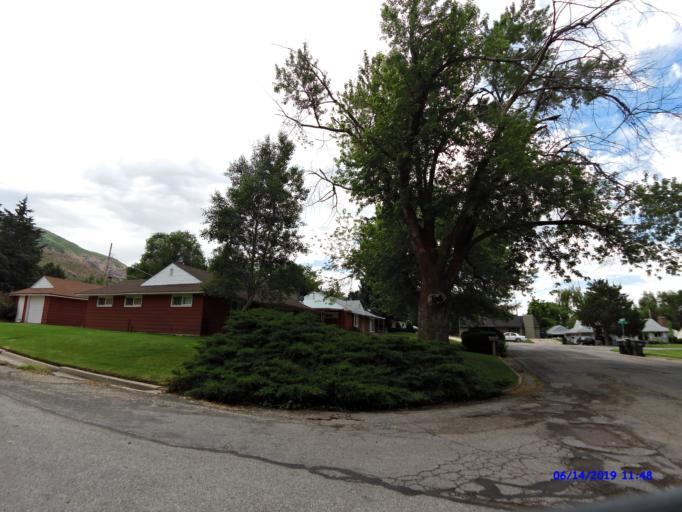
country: US
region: Utah
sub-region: Weber County
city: Ogden
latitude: 41.2554
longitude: -111.9437
